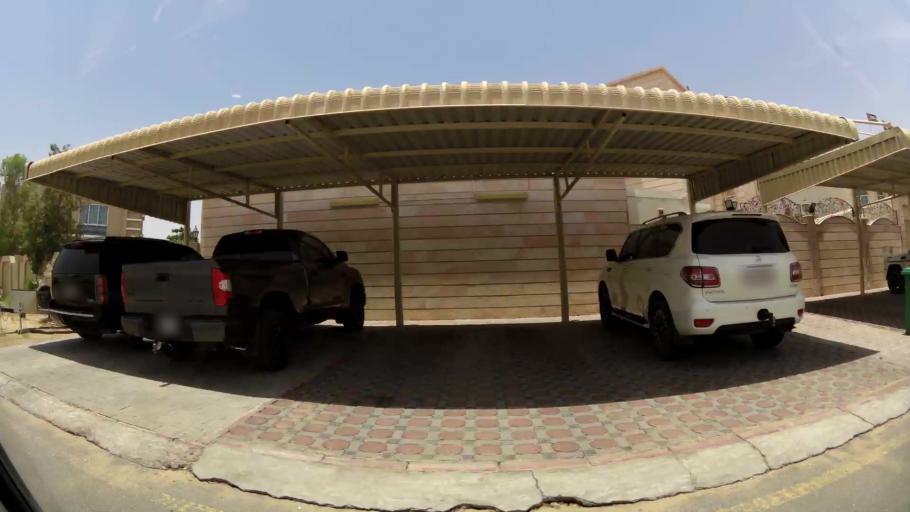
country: AE
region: Ash Shariqah
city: Sharjah
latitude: 25.2342
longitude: 55.4636
